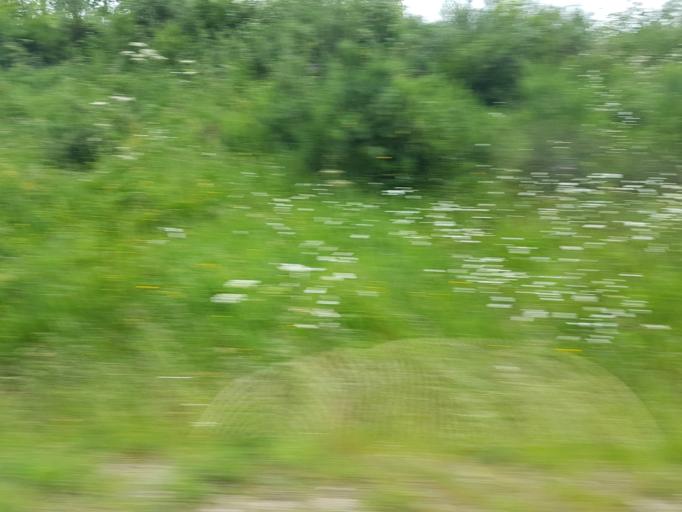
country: FR
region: Bourgogne
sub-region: Departement de la Nievre
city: Chateau-Chinon(Ville)
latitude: 47.0494
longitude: 3.9943
